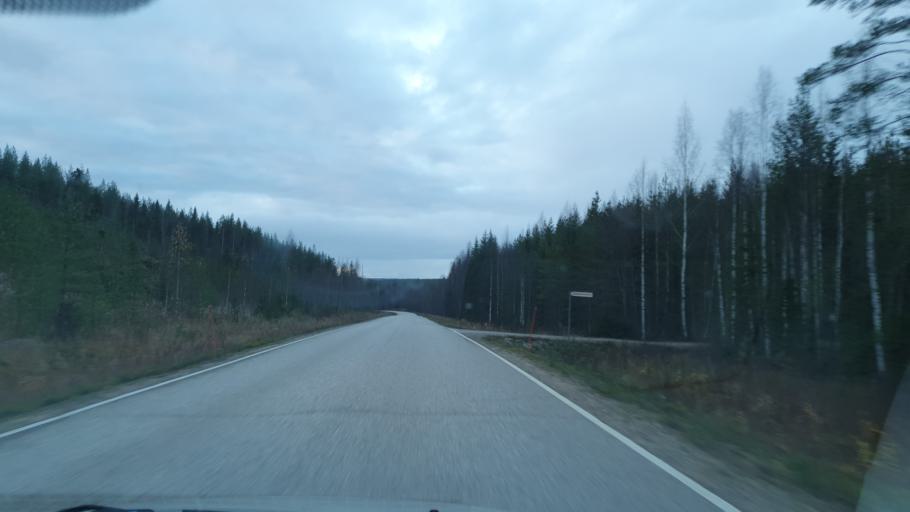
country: FI
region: Kainuu
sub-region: Kajaani
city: Ristijaervi
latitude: 64.4260
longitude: 28.3935
